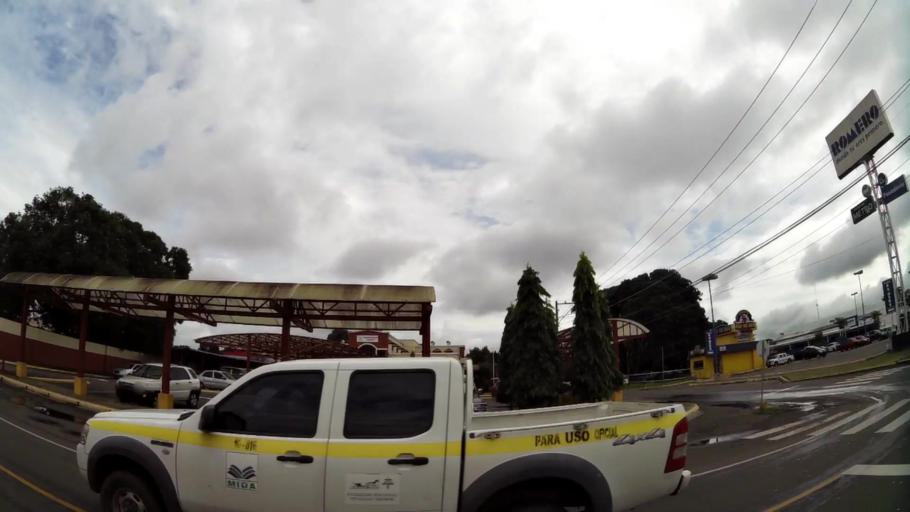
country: PA
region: Chiriqui
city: David
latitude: 8.4266
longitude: -82.4360
